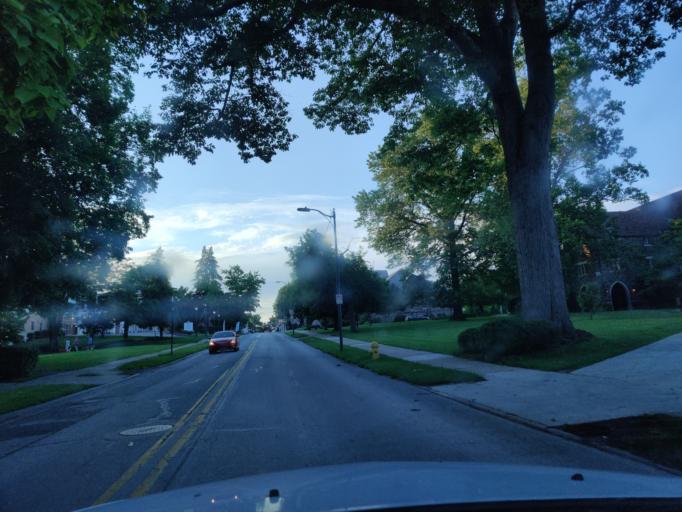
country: US
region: Pennsylvania
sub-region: Lawrence County
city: New Wilmington
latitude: 41.1193
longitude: -80.3331
